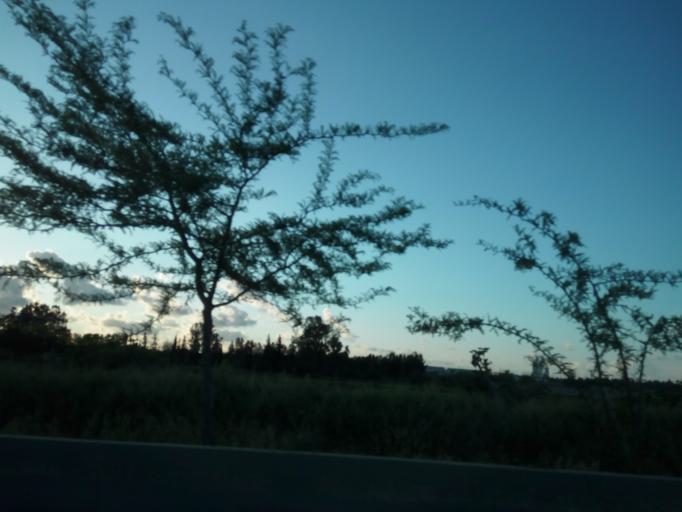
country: DZ
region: Tipaza
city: Baraki
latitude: 36.6901
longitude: 3.1200
